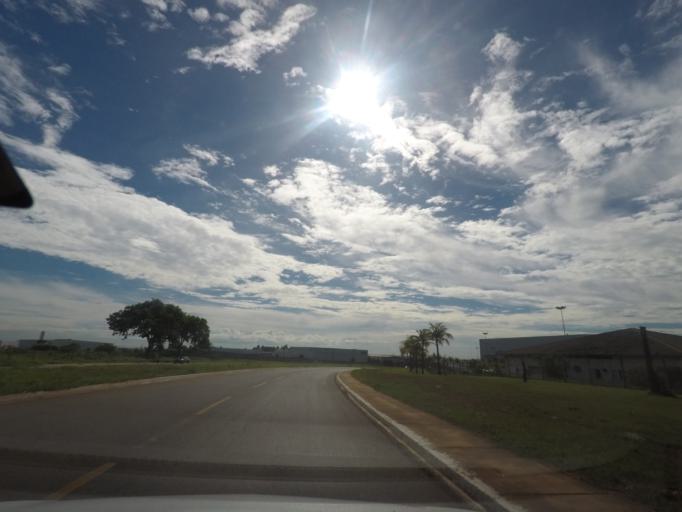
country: BR
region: Goias
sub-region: Aparecida De Goiania
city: Aparecida de Goiania
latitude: -16.8079
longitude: -49.2721
